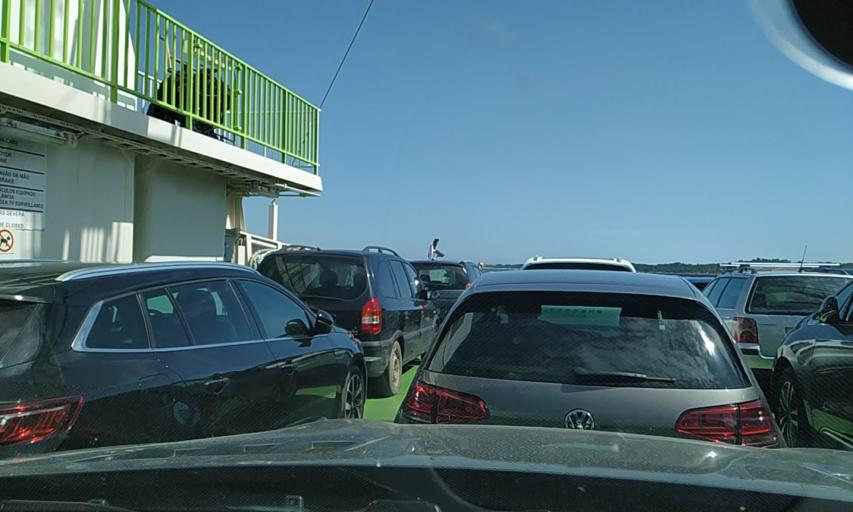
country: PT
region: Setubal
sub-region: Setubal
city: Setubal
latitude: 38.4816
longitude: -8.8733
